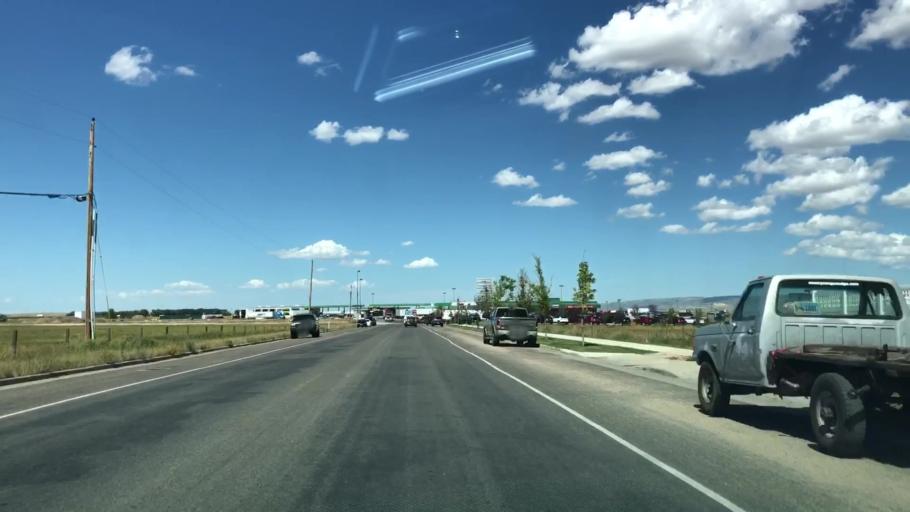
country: US
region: Wyoming
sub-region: Albany County
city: Laramie
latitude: 41.3253
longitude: -105.6203
